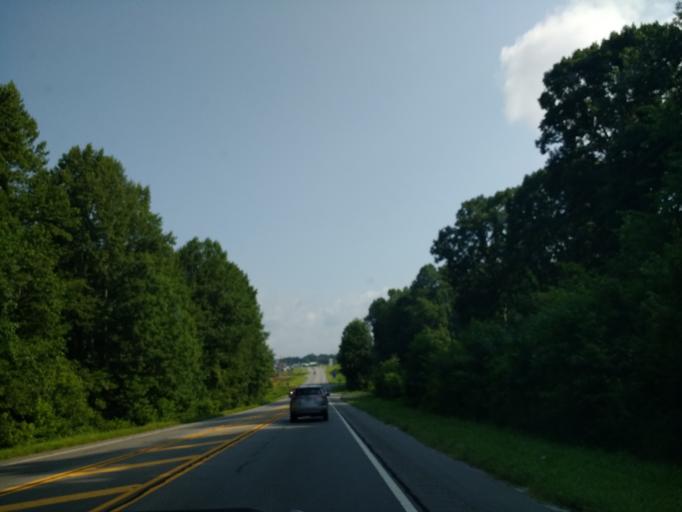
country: US
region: Georgia
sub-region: White County
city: Cleveland
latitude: 34.5499
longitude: -83.7608
